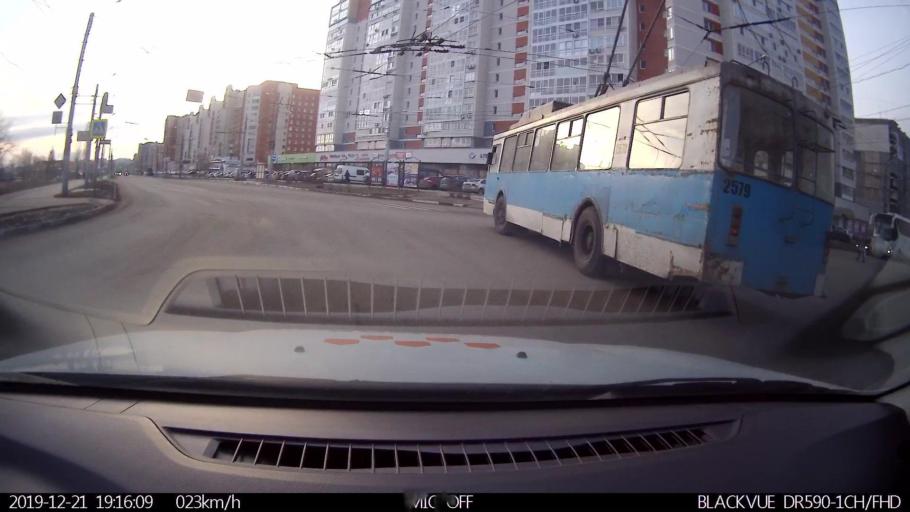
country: RU
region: Nizjnij Novgorod
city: Nizhniy Novgorod
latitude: 56.3410
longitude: 43.9296
